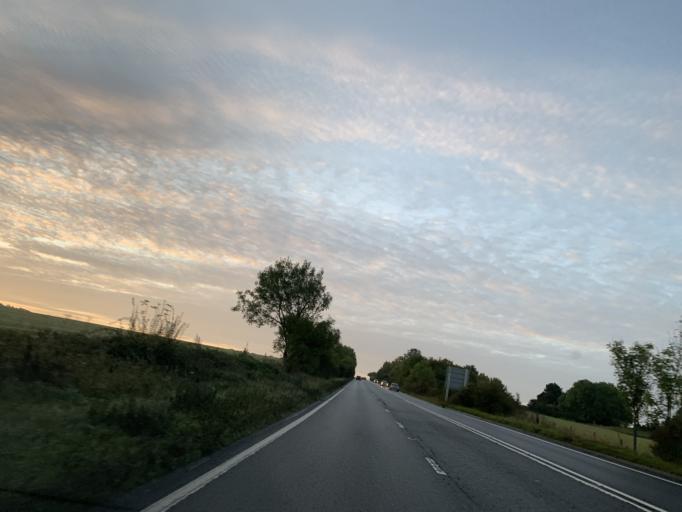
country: GB
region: England
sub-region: Wiltshire
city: Alderbury
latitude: 51.0309
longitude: -1.7159
